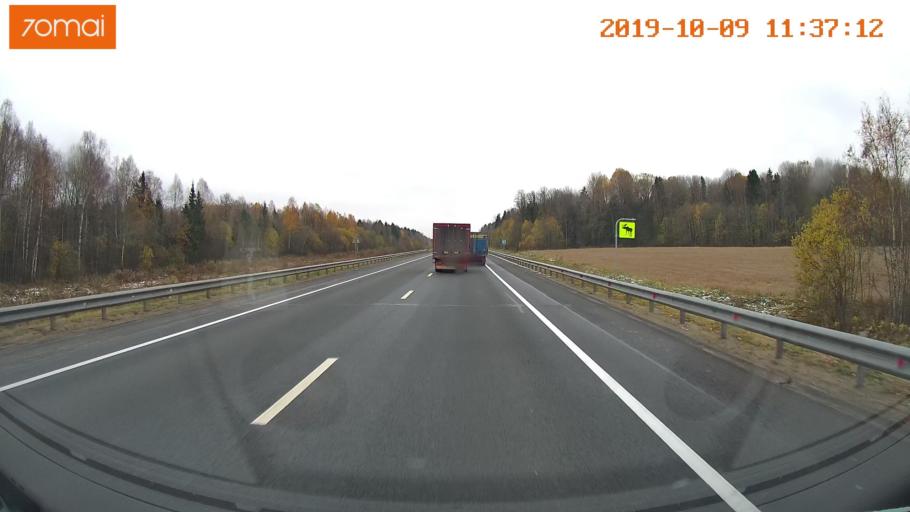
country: RU
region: Vologda
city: Gryazovets
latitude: 58.9817
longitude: 40.1439
